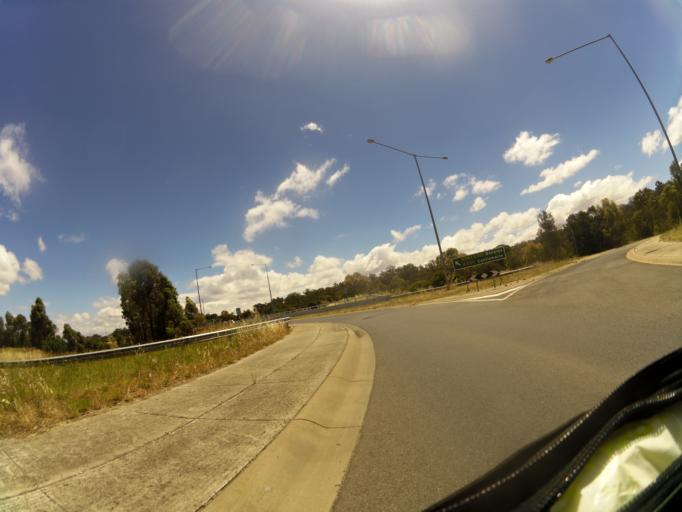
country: AU
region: Victoria
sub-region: Mount Alexander
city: Castlemaine
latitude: -37.0034
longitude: 144.2502
